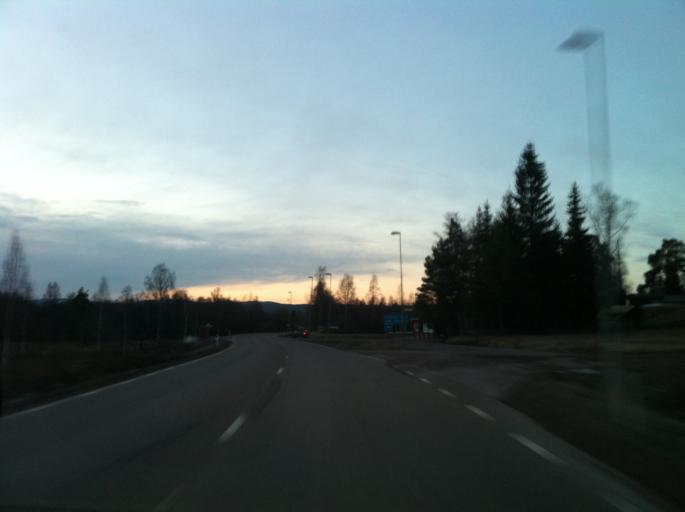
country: SE
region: Dalarna
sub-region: Orsa Kommun
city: Orsa
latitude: 61.1060
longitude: 14.6322
